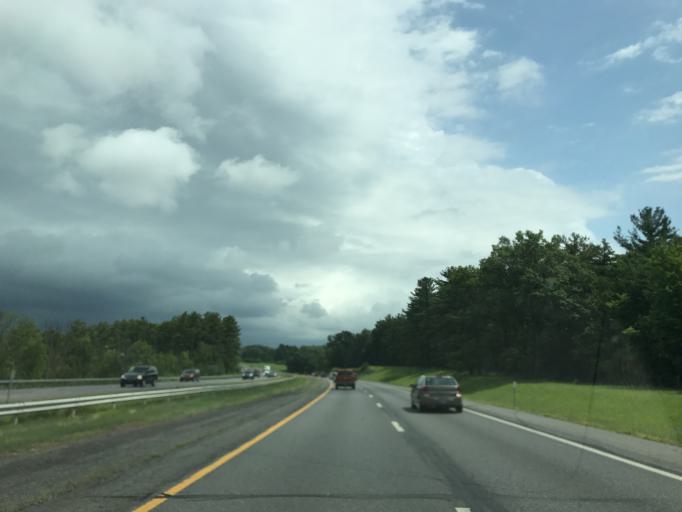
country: US
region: New York
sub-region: Albany County
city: Ravena
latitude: 42.4106
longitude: -73.8126
